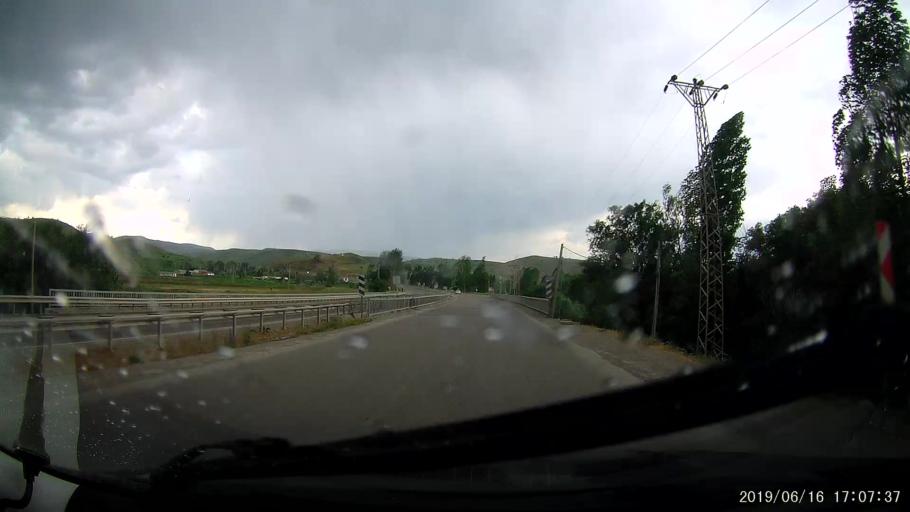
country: TR
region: Erzurum
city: Askale
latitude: 39.9171
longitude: 40.6723
